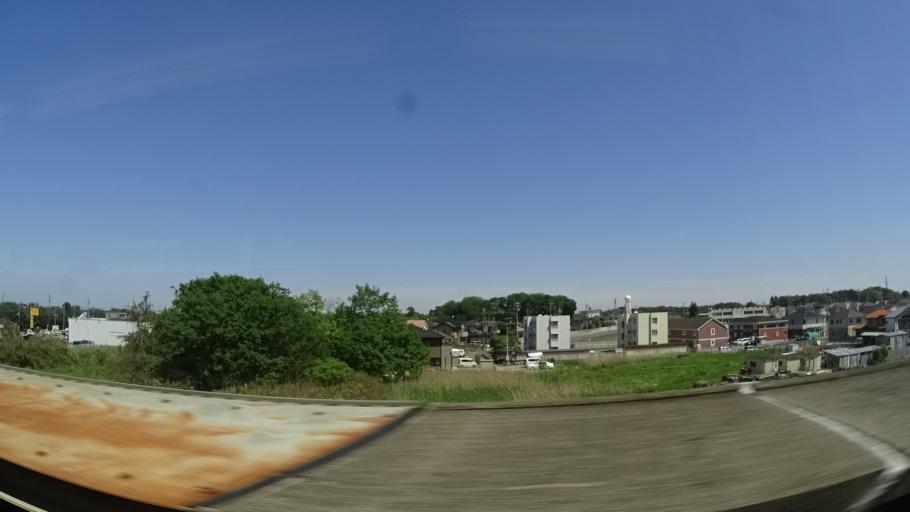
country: JP
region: Ibaraki
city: Koga
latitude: 36.1930
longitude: 139.7445
